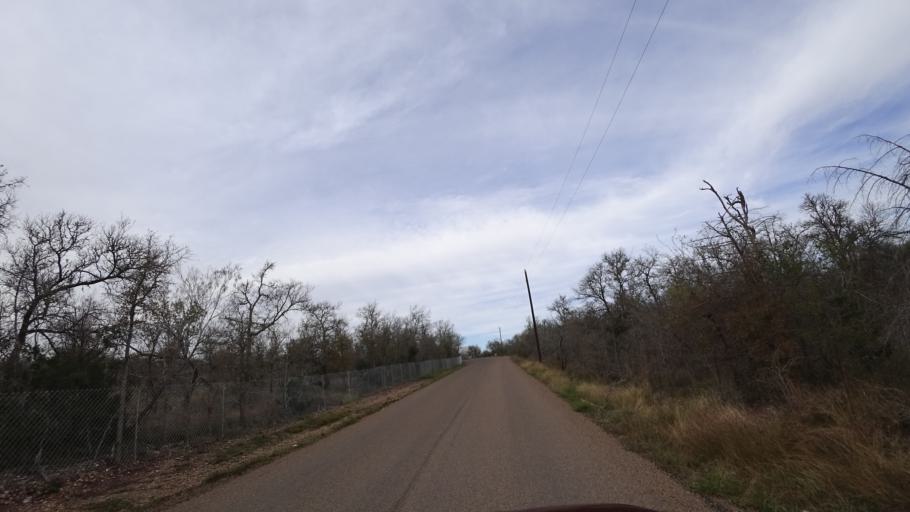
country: US
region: Texas
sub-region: Travis County
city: Garfield
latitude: 30.1132
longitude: -97.5670
